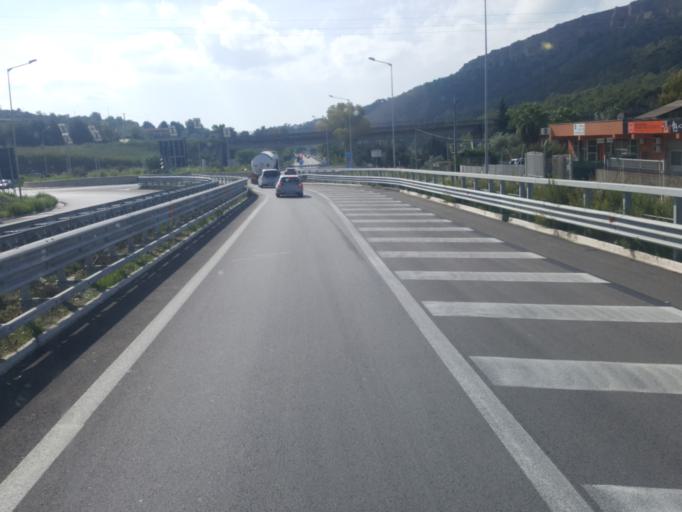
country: IT
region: Sicily
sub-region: Agrigento
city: Agrigento
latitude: 37.3107
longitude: 13.6081
